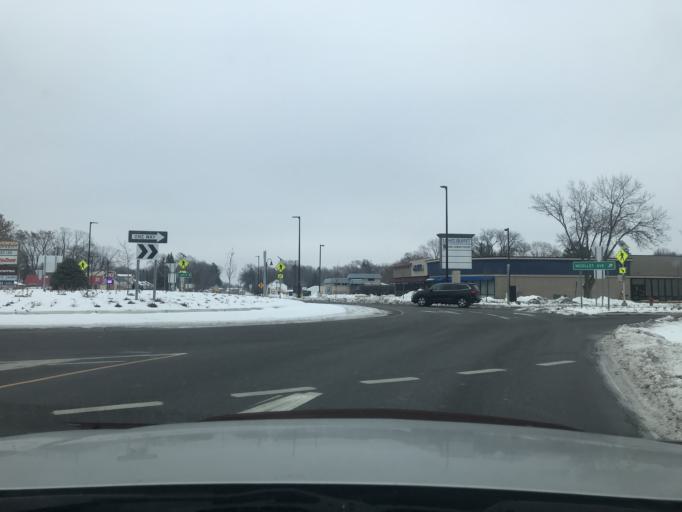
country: US
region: Minnesota
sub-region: Hennepin County
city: Richfield
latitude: 44.8834
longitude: -93.2786
